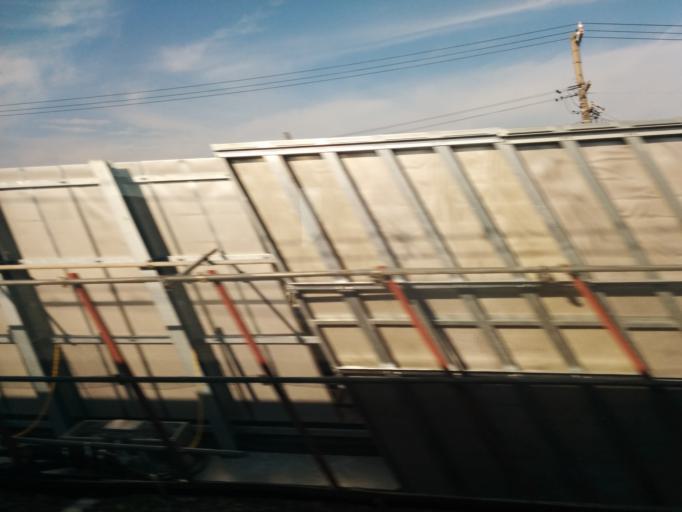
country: JP
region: Aichi
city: Inazawa
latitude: 35.2265
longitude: 136.8110
